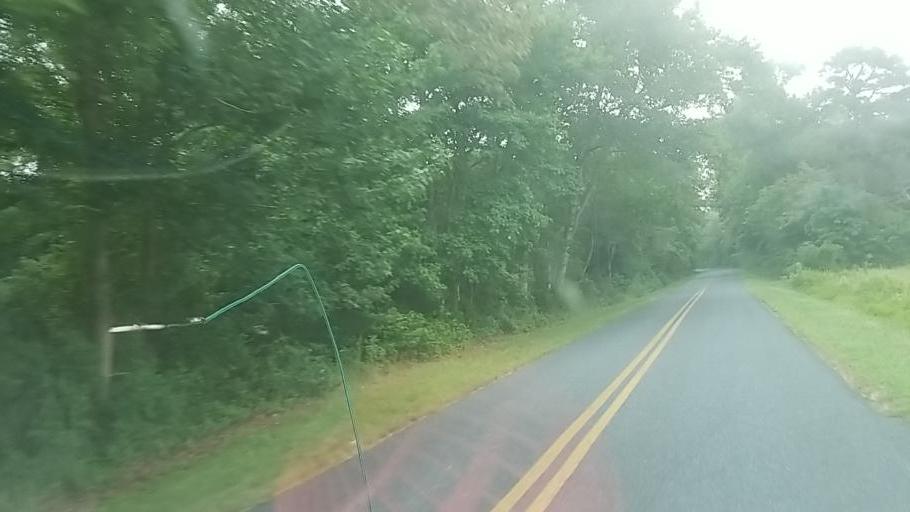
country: US
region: Maryland
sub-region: Wicomico County
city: Pittsville
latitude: 38.4146
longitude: -75.4892
